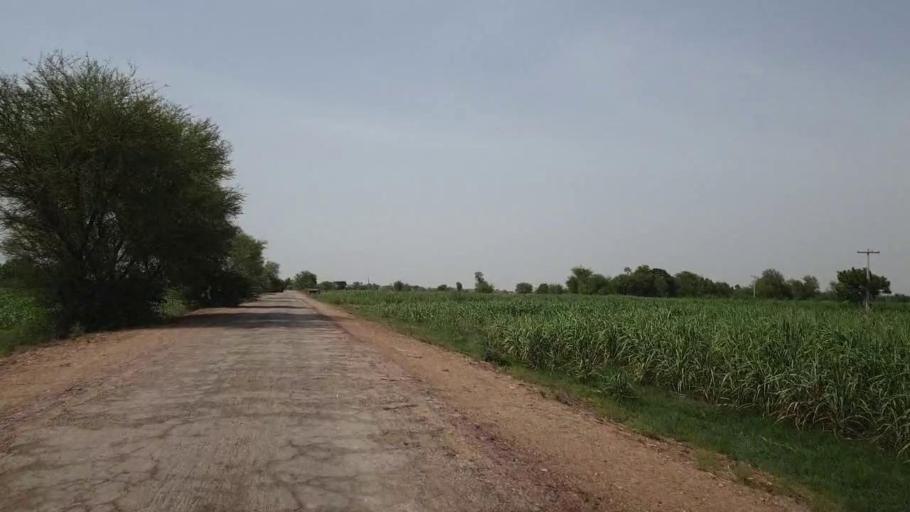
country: PK
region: Sindh
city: Daur
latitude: 26.5341
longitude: 68.4076
